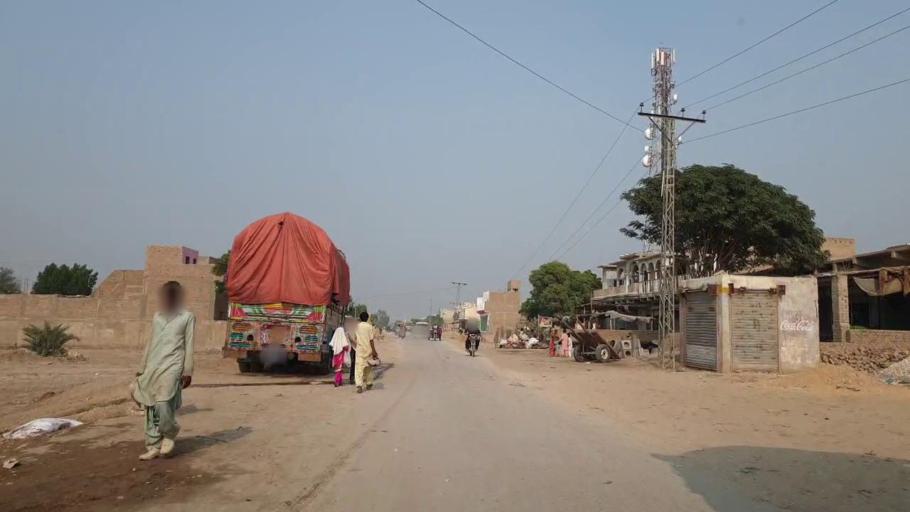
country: PK
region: Sindh
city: Bhan
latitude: 26.5636
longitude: 67.7233
